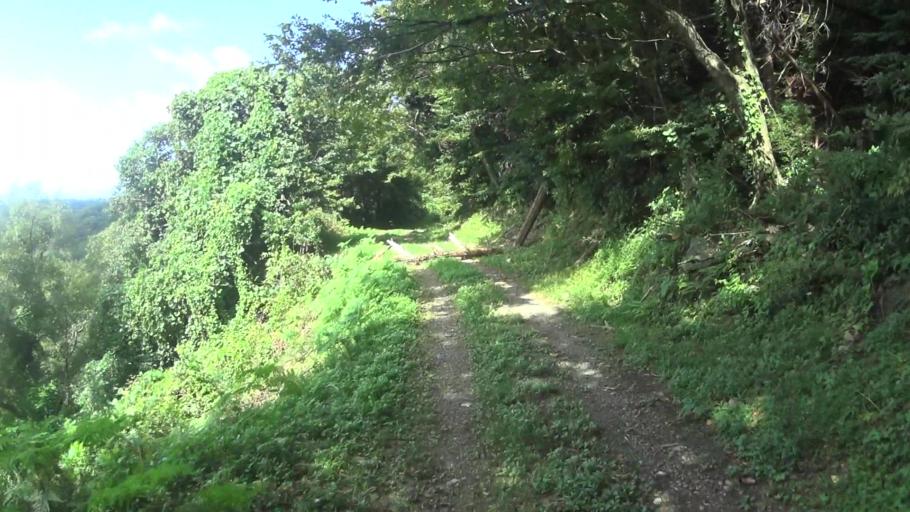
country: JP
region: Kyoto
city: Miyazu
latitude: 35.7429
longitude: 135.1974
